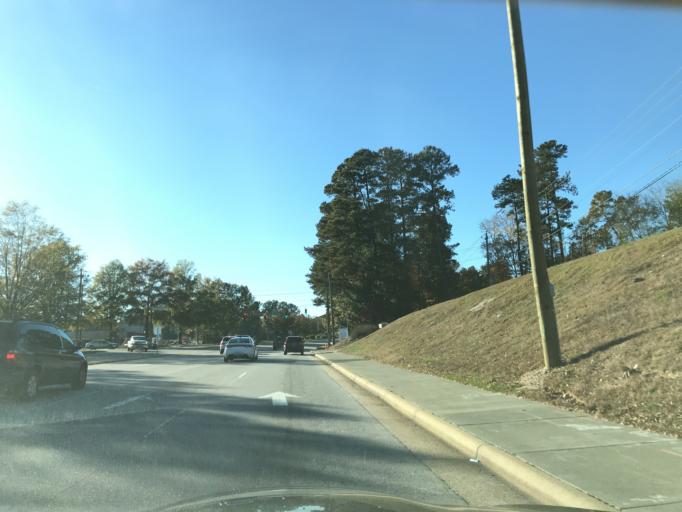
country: US
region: North Carolina
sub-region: Wake County
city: Raleigh
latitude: 35.7680
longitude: -78.5766
